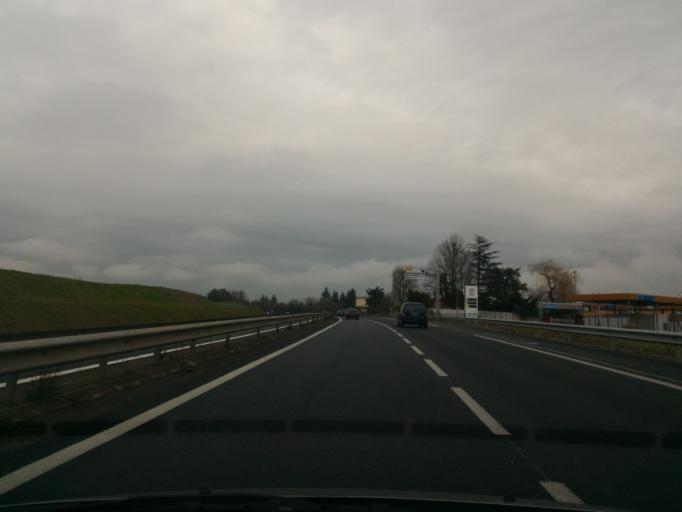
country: FR
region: Poitou-Charentes
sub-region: Departement de la Vienne
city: Vivonne
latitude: 46.4317
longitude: 0.2621
